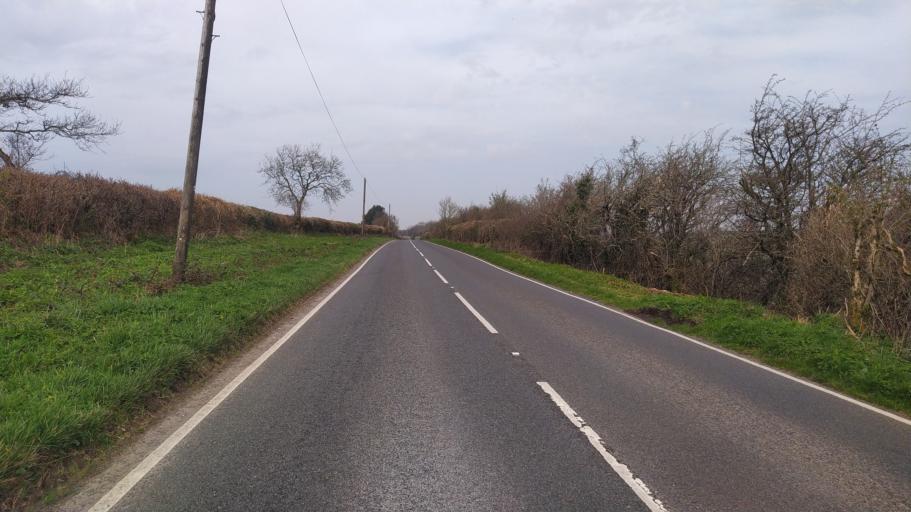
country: GB
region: England
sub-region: Dorset
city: Beaminster
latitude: 50.7847
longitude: -2.6118
